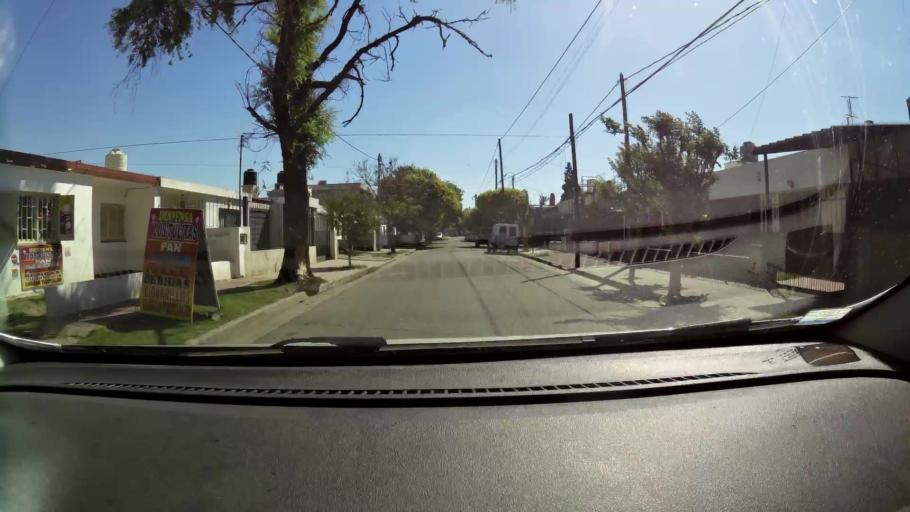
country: AR
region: Cordoba
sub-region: Departamento de Capital
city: Cordoba
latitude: -31.3743
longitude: -64.1689
